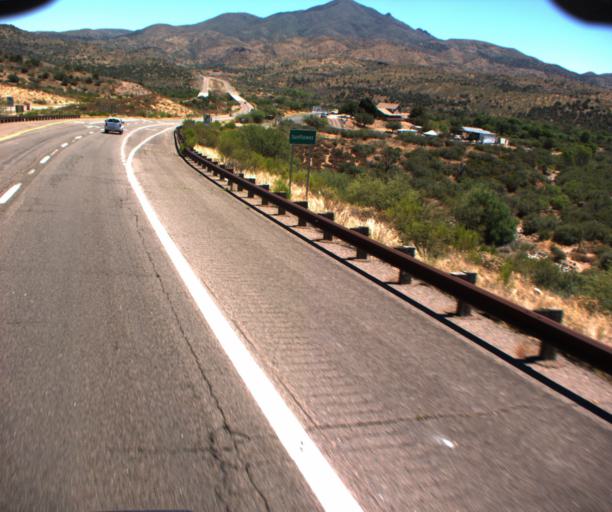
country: US
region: Arizona
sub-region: Gila County
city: Tonto Basin
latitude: 33.8622
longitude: -111.4733
